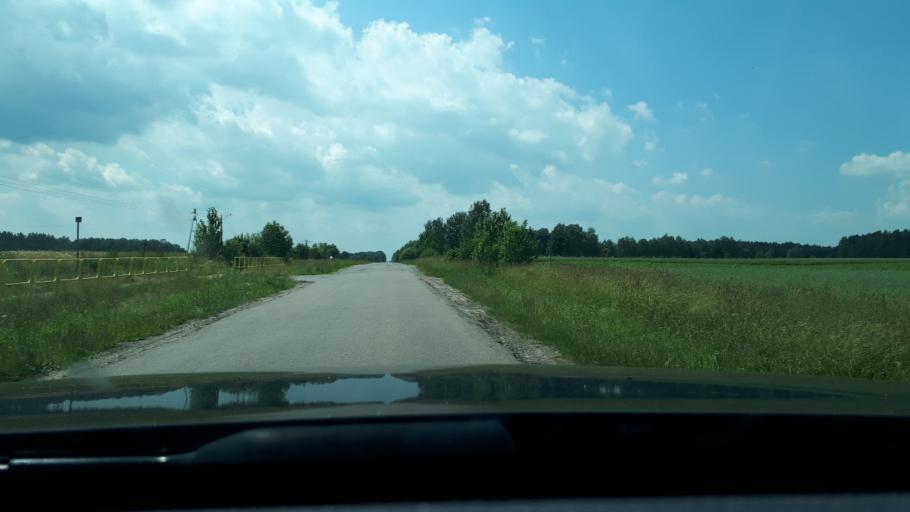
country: PL
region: Podlasie
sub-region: Powiat bialostocki
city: Choroszcz
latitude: 53.1236
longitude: 22.9408
